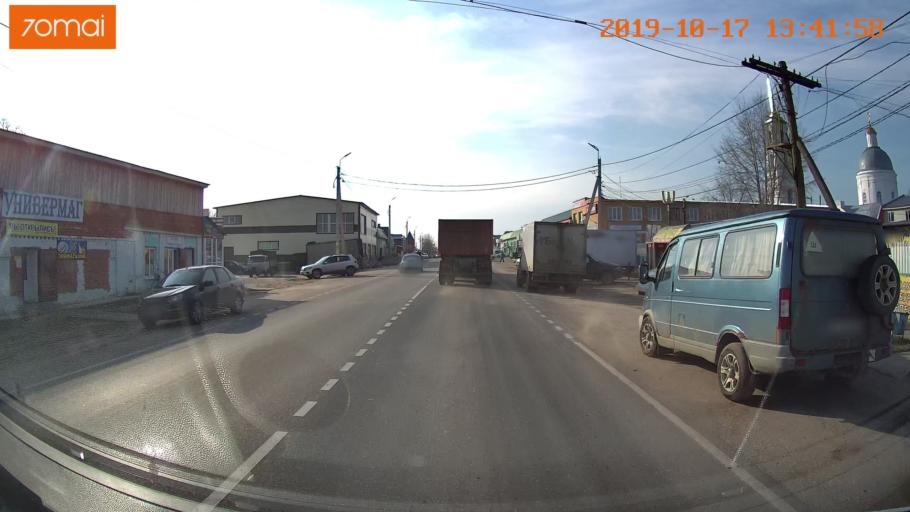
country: RU
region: Rjazan
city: Tuma
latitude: 55.1481
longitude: 40.5580
